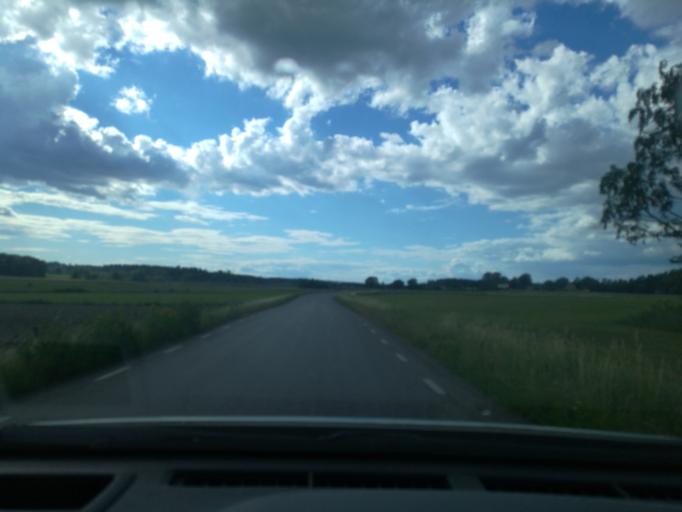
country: SE
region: Soedermanland
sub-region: Eskilstuna Kommun
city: Arla
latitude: 59.4505
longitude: 16.7388
